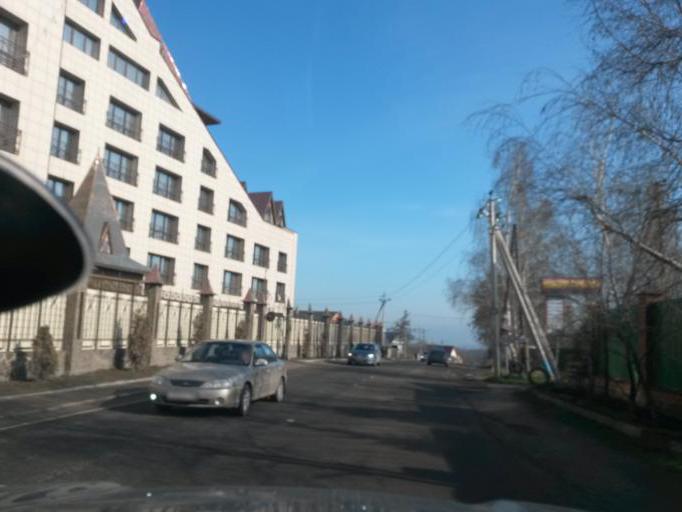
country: RU
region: Moscow
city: Zyablikovo
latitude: 55.6112
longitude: 37.7839
